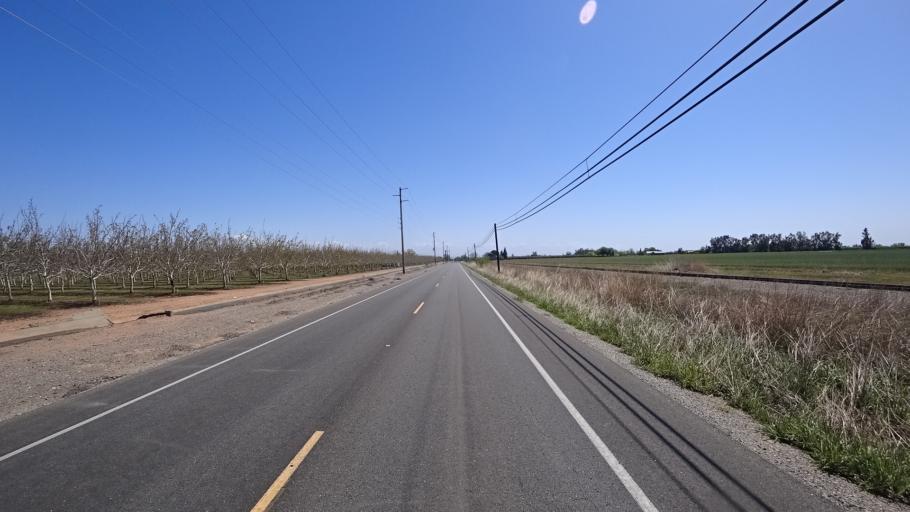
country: US
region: California
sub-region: Glenn County
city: Orland
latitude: 39.7689
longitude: -122.1754
